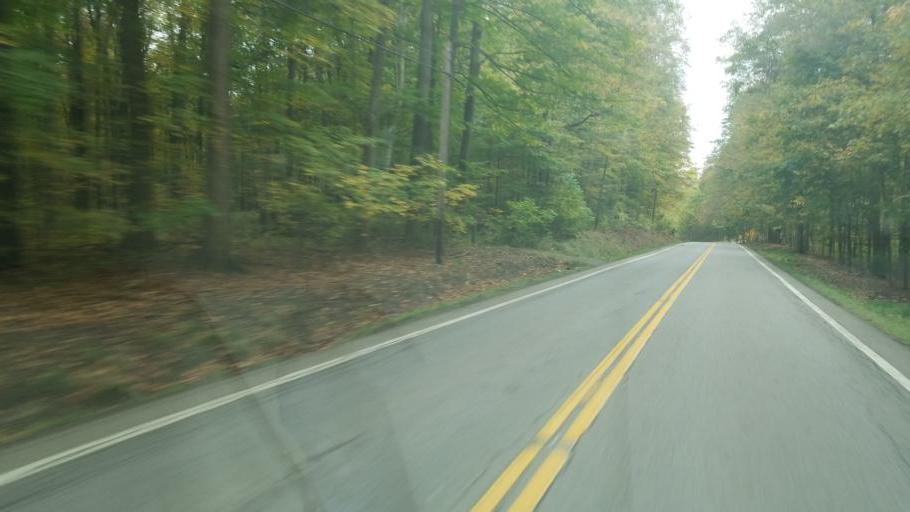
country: US
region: Ohio
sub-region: Richland County
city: Lincoln Heights
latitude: 40.7103
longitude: -82.3984
